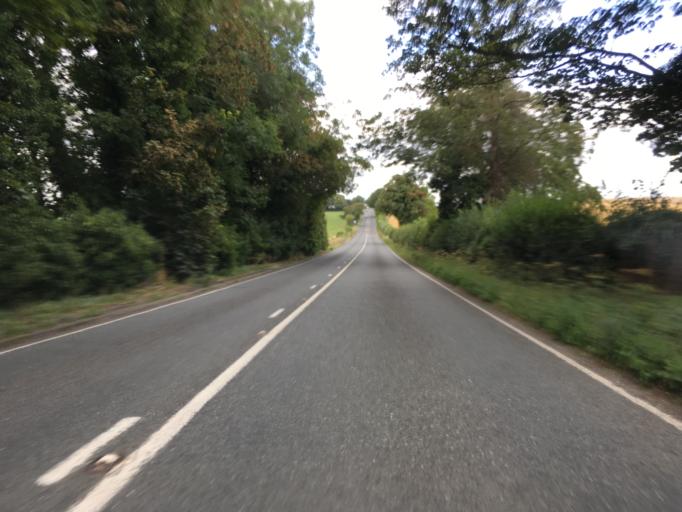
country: GB
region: England
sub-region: Hampshire
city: Kings Worthy
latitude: 51.0973
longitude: -1.2886
